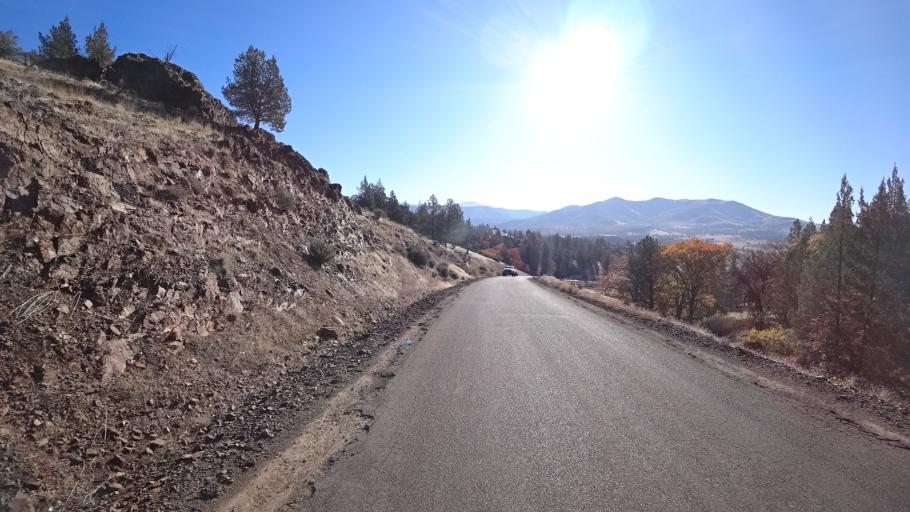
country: US
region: California
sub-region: Siskiyou County
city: Montague
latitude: 41.9018
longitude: -122.4262
